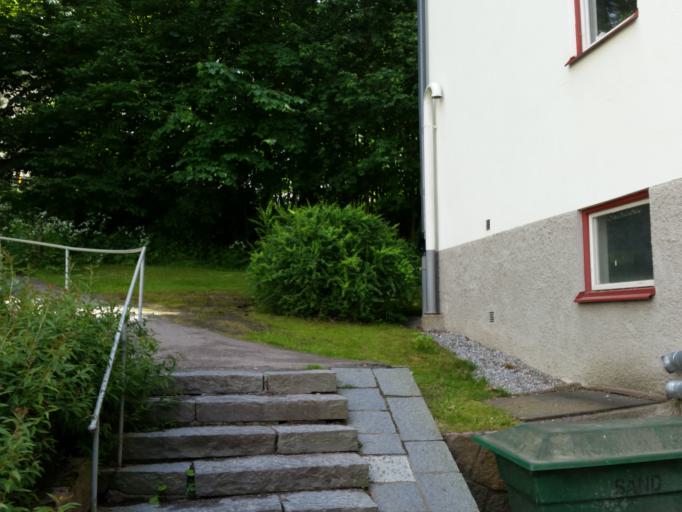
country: SE
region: Stockholm
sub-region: Solna Kommun
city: Solna
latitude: 59.3684
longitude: 17.9988
